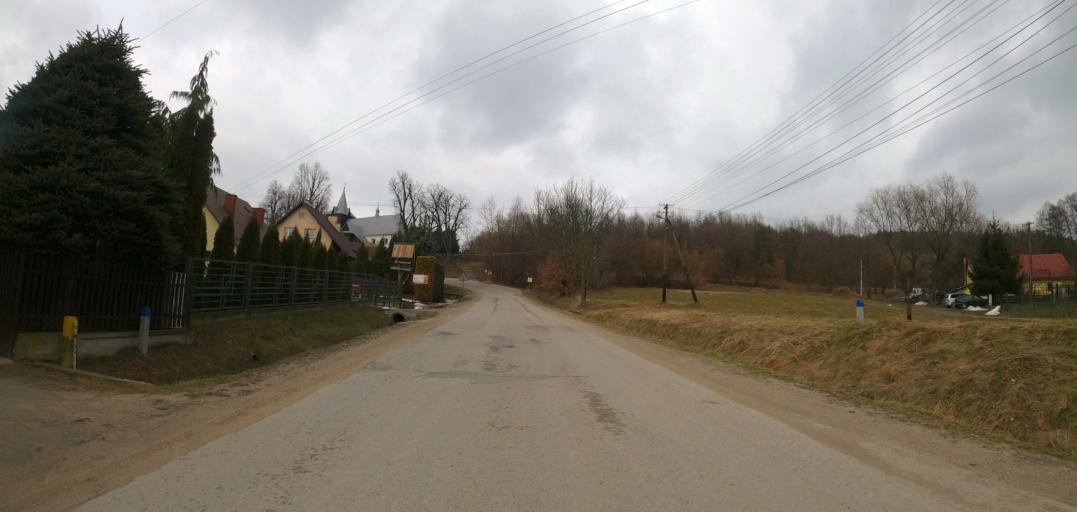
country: PL
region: Subcarpathian Voivodeship
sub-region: Powiat debicki
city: Pilzno
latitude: 49.9852
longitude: 21.3390
